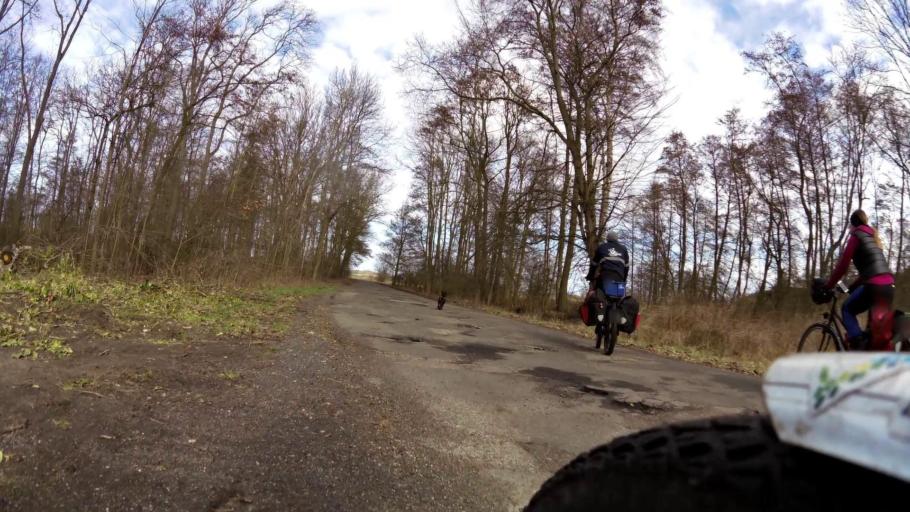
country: PL
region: West Pomeranian Voivodeship
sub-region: Powiat kamienski
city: Kamien Pomorski
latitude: 53.9837
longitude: 14.7693
